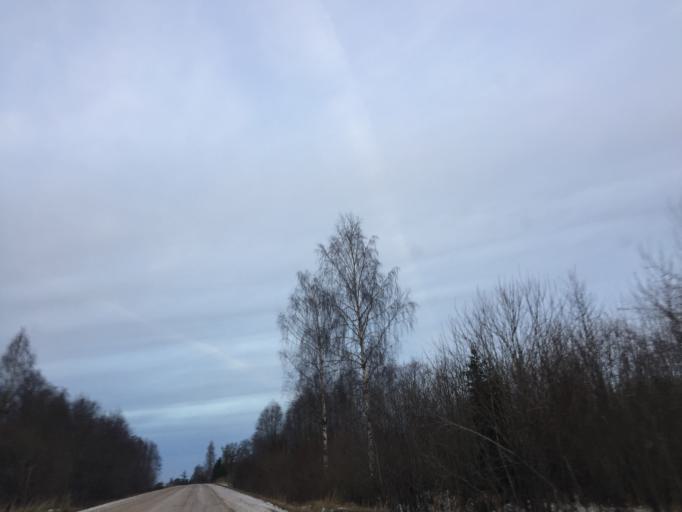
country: LV
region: Limbazu Rajons
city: Limbazi
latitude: 57.5782
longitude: 24.8289
